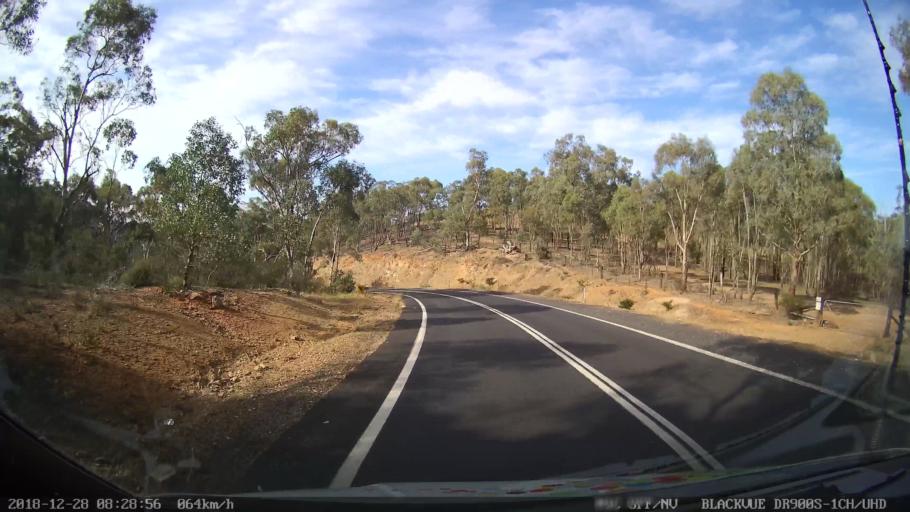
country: AU
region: New South Wales
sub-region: Blayney
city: Blayney
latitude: -33.9449
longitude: 149.3240
